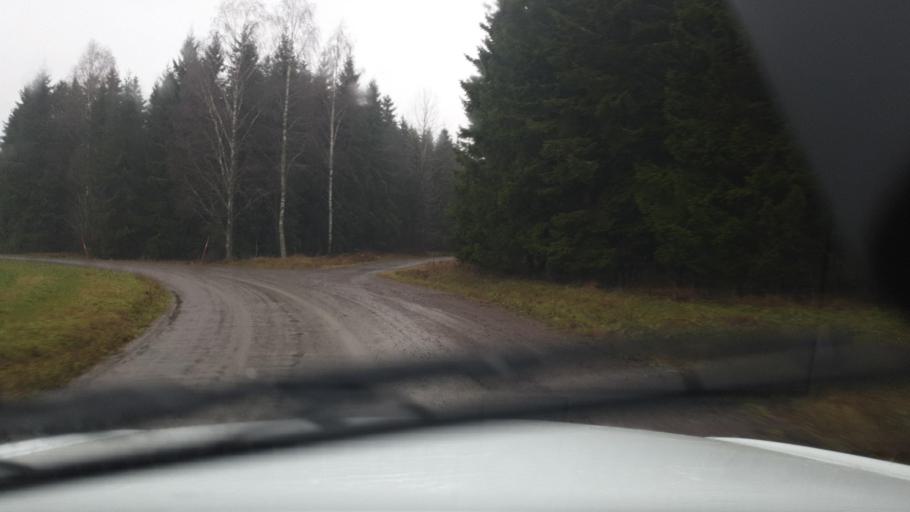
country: SE
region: Vaermland
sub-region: Sunne Kommun
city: Sunne
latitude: 59.8032
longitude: 13.0969
